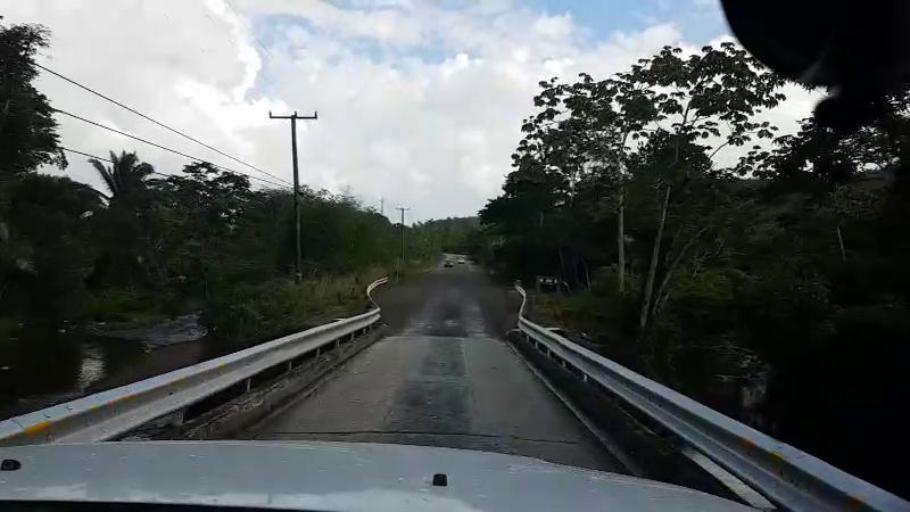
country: BZ
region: Cayo
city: Belmopan
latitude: 17.0898
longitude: -88.6206
